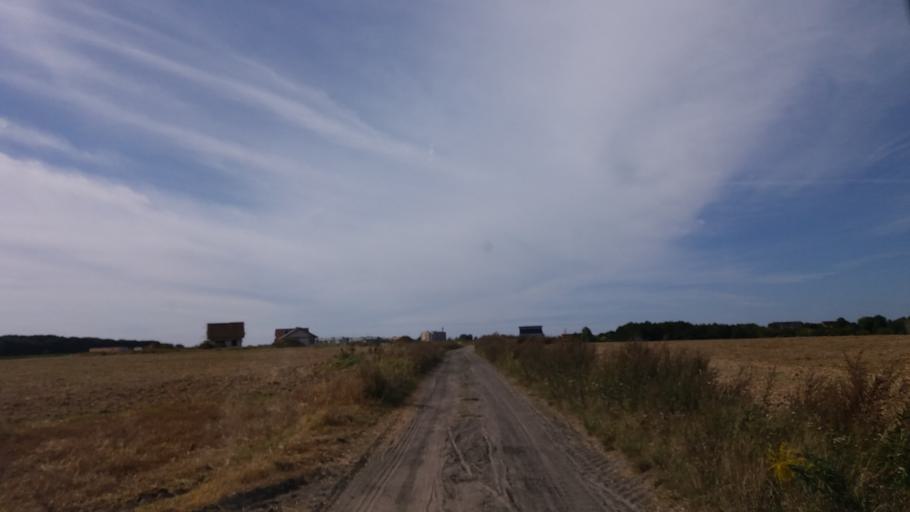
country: PL
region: West Pomeranian Voivodeship
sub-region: Powiat choszczenski
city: Choszczno
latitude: 53.1578
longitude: 15.4459
